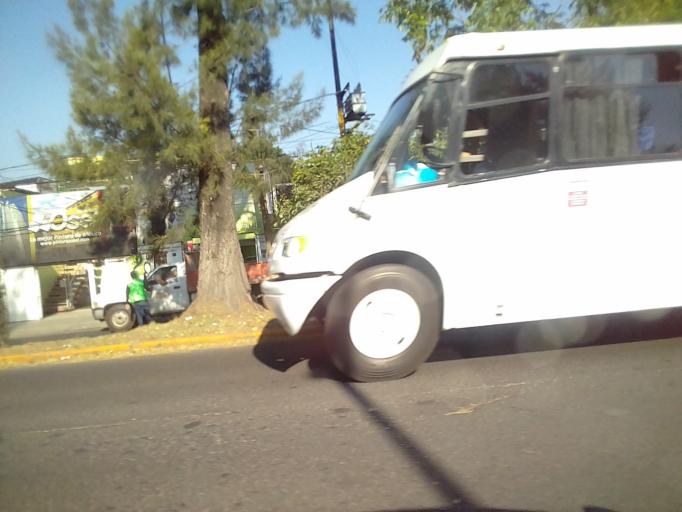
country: MX
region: Mexico
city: Naucalpan de Juarez
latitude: 19.4903
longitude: -99.2281
